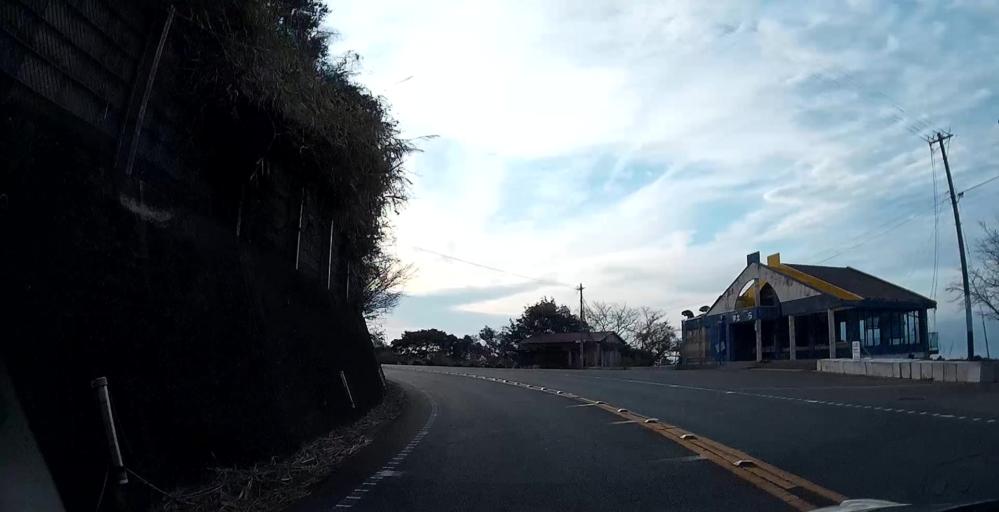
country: JP
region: Kumamoto
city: Matsubase
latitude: 32.6538
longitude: 130.5001
